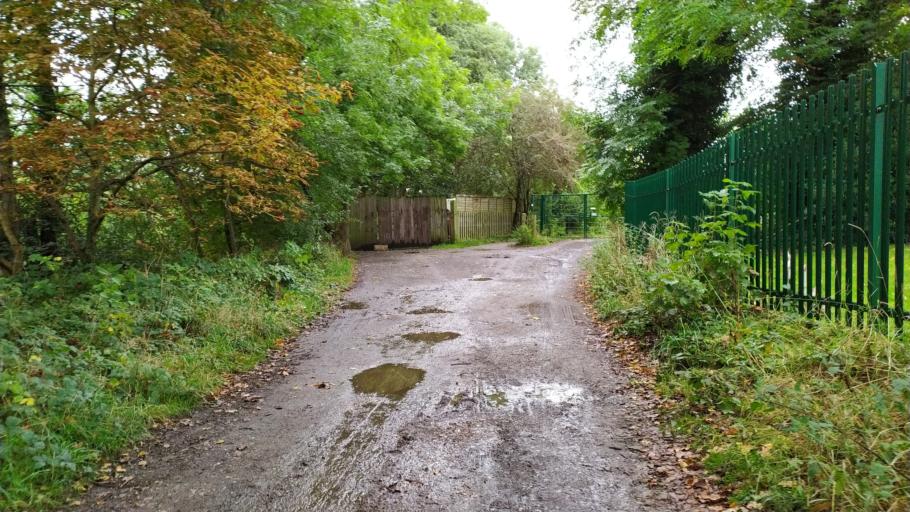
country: GB
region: England
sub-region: City and Borough of Leeds
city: Chapel Allerton
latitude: 53.8298
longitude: -1.5739
